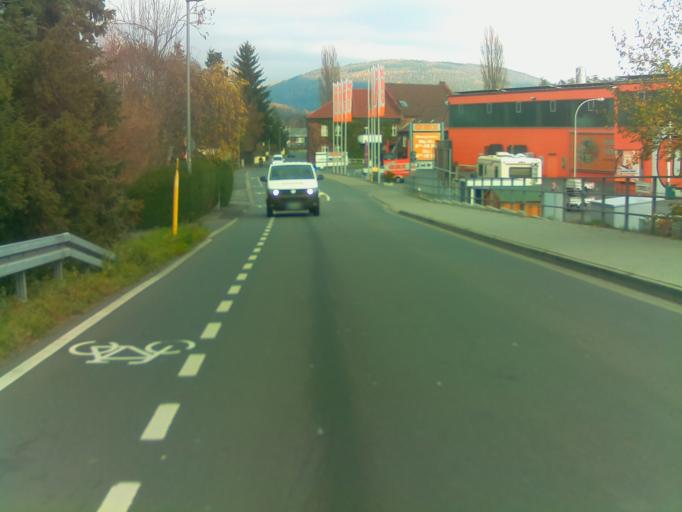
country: DE
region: Bavaria
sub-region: Regierungsbezirk Unterfranken
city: Kleinheubach
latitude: 49.7015
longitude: 9.2242
